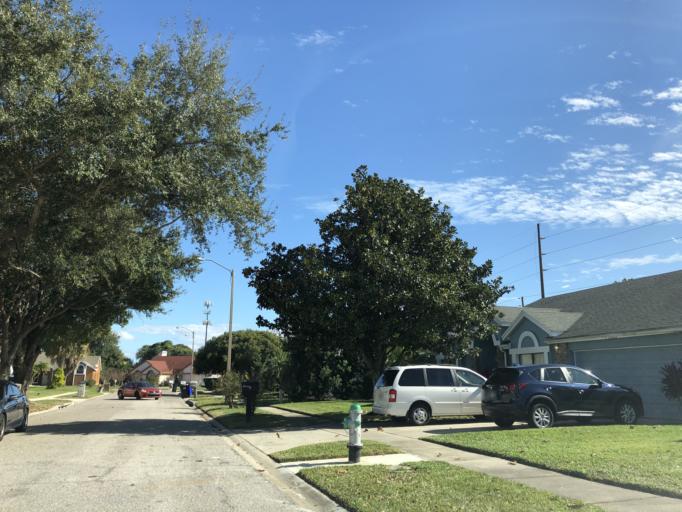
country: US
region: Florida
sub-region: Orange County
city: Hunters Creek
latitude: 28.3768
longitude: -81.4081
